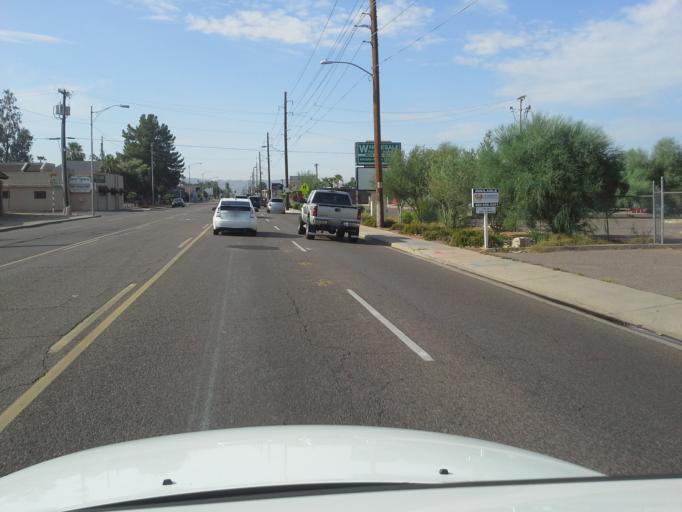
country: US
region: Arizona
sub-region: Maricopa County
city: Phoenix
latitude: 33.4925
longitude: -112.0477
